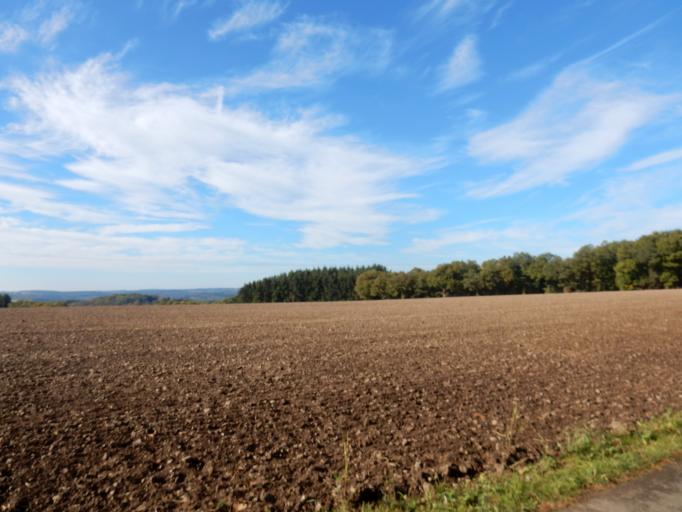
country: LU
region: Diekirch
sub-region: Canton de Wiltz
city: Bavigne
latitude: 49.9165
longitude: 5.8831
